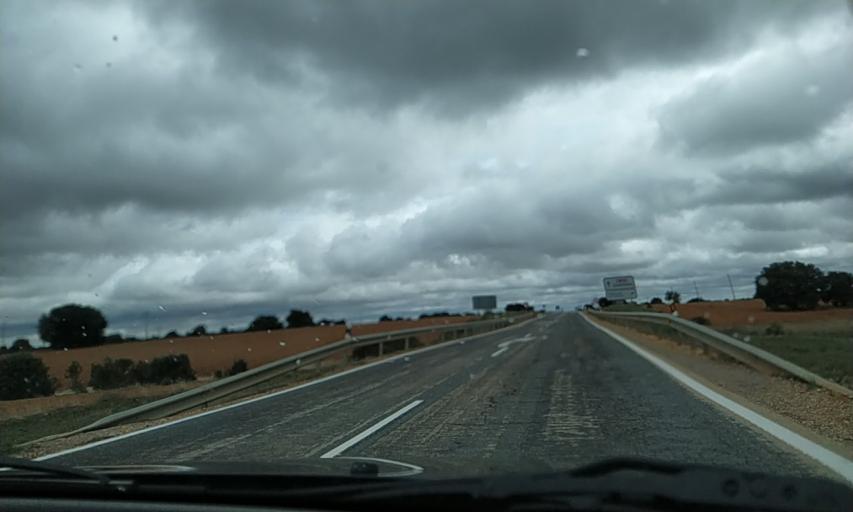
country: ES
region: Castille and Leon
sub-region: Provincia de Zamora
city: Perilla de Castro
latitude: 41.7375
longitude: -5.8300
